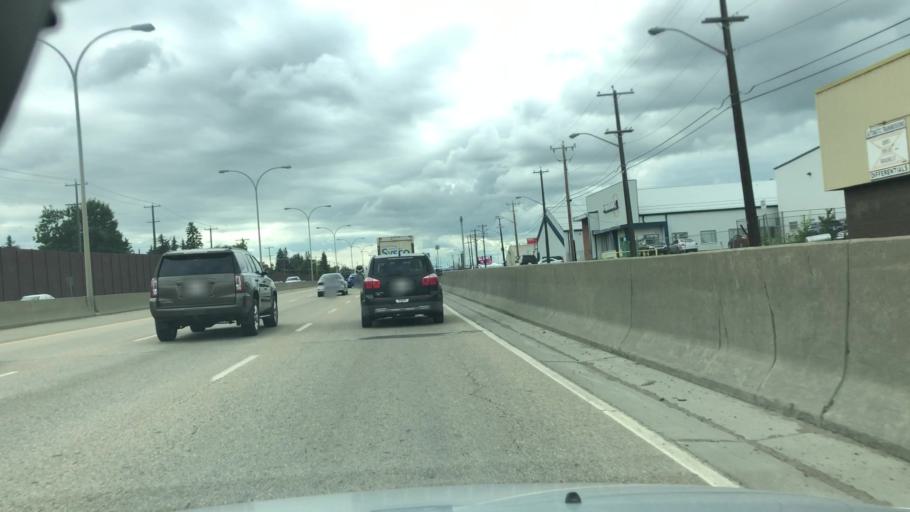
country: CA
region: Alberta
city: Edmonton
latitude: 53.5814
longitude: -113.4826
